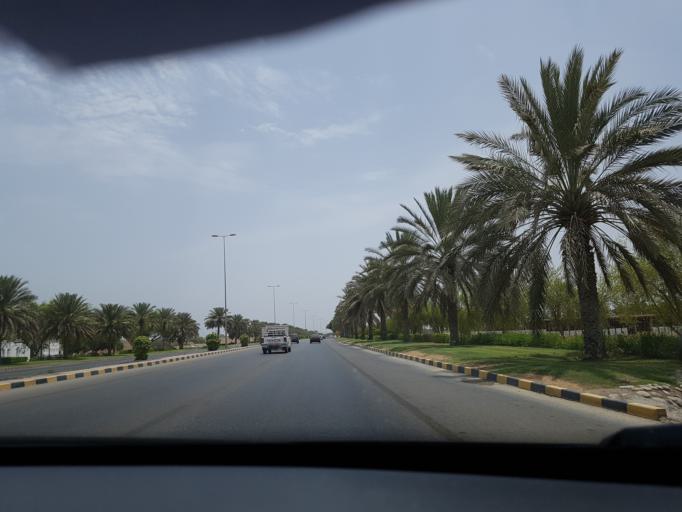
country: OM
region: Muhafazat Masqat
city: As Sib al Jadidah
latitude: 23.6925
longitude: 58.0724
